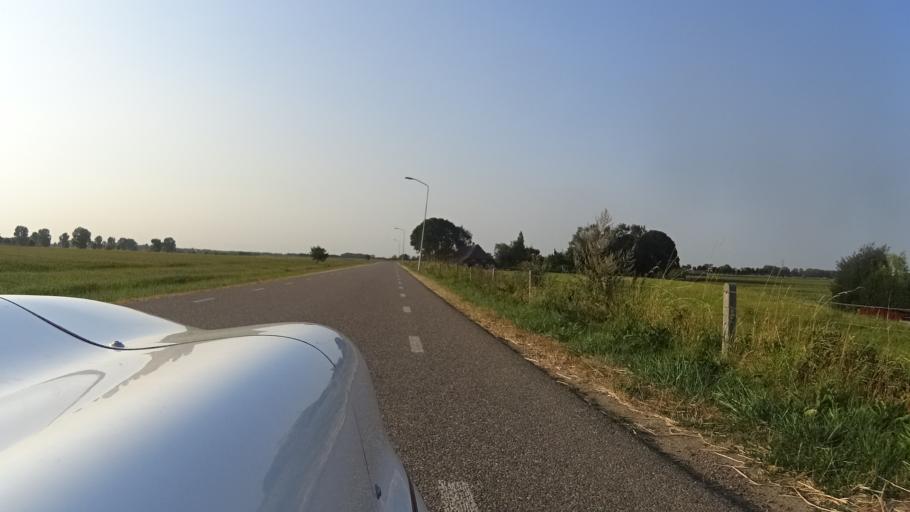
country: NL
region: Gelderland
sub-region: Gemeente Wijchen
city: Bergharen
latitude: 51.8038
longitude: 5.6571
